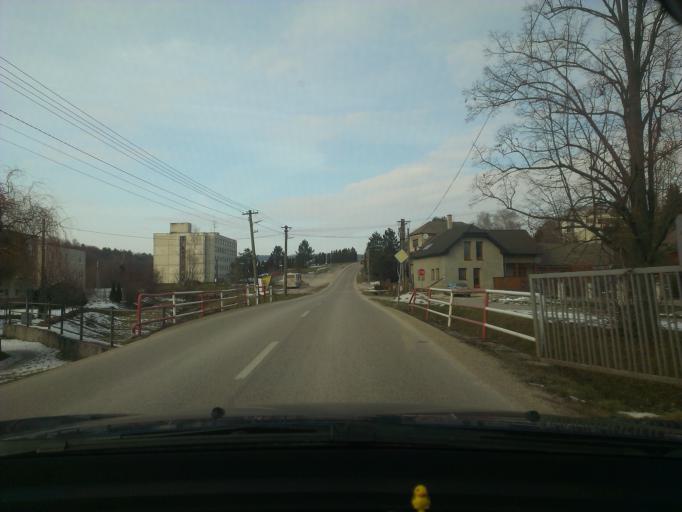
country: SK
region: Nitriansky
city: Stara Tura
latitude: 48.7054
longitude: 17.6845
